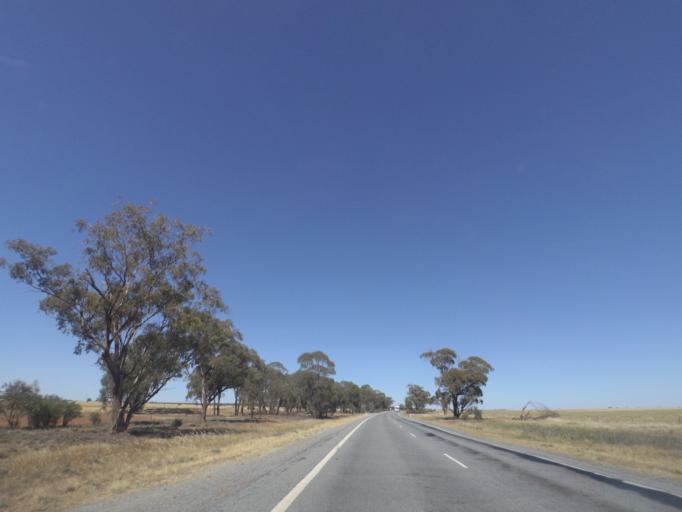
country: AU
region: New South Wales
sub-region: Narrandera
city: Narrandera
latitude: -34.4117
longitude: 146.8758
